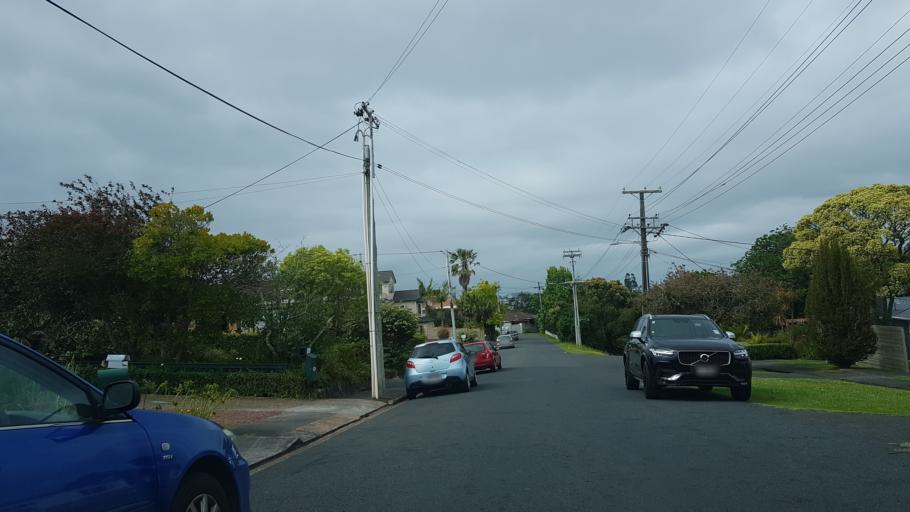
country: NZ
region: Auckland
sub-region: Auckland
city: North Shore
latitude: -36.8061
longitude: 174.7473
